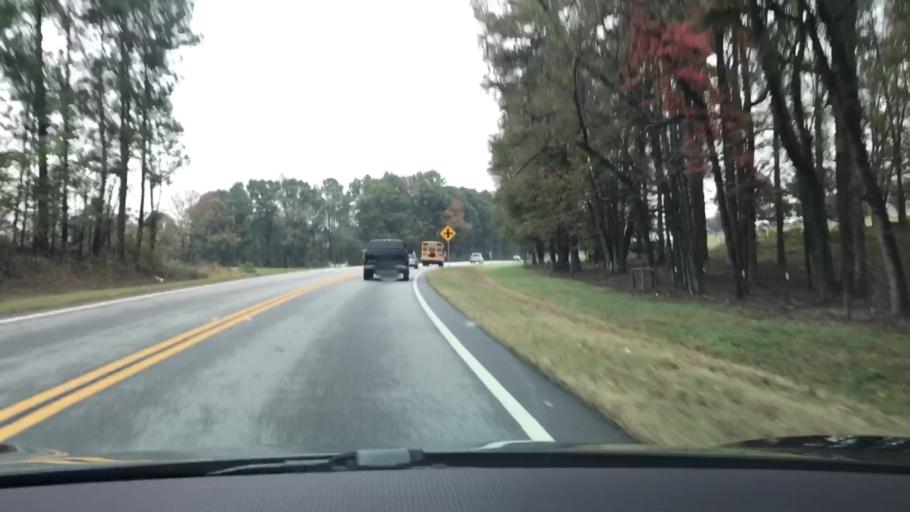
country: US
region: Georgia
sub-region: Greene County
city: Greensboro
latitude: 33.6059
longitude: -83.1995
